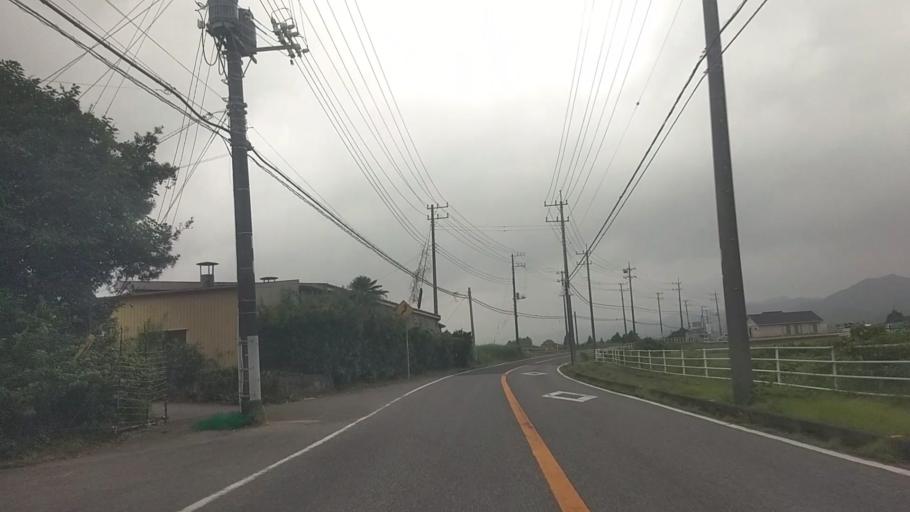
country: JP
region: Chiba
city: Kawaguchi
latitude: 35.1234
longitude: 140.0618
